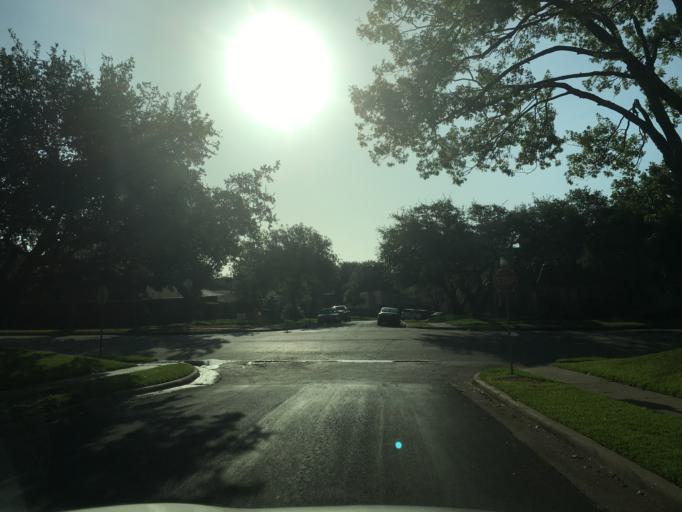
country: US
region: Texas
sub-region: Dallas County
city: Richardson
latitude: 32.8875
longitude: -96.7371
